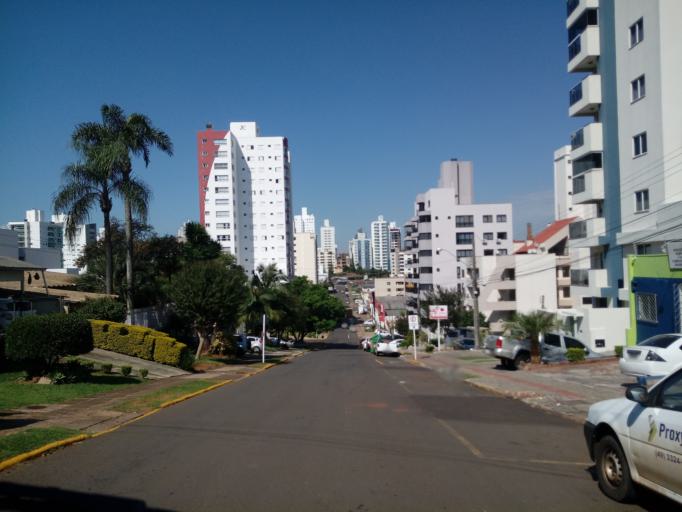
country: BR
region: Santa Catarina
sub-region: Chapeco
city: Chapeco
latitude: -27.0957
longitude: -52.6117
